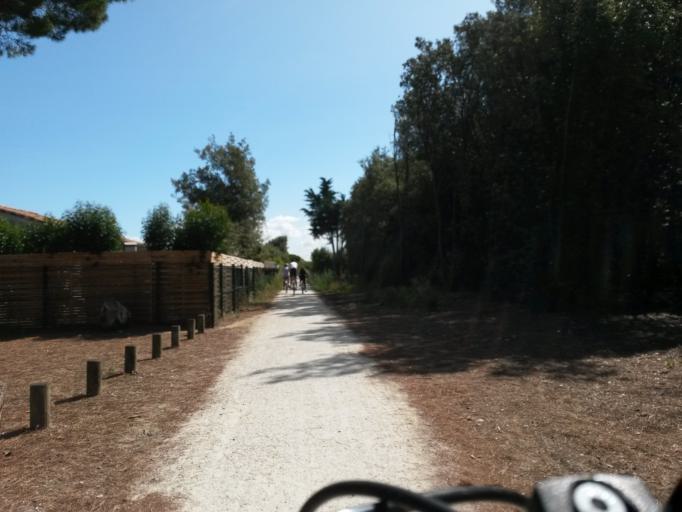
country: FR
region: Poitou-Charentes
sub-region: Departement de la Charente-Maritime
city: La Flotte
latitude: 46.1878
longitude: -1.3422
